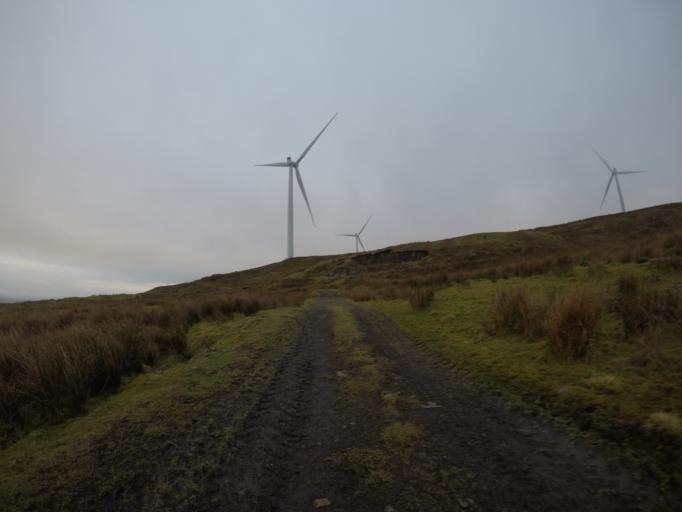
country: GB
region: Scotland
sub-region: North Ayrshire
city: Dalry
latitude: 55.7379
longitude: -4.7704
